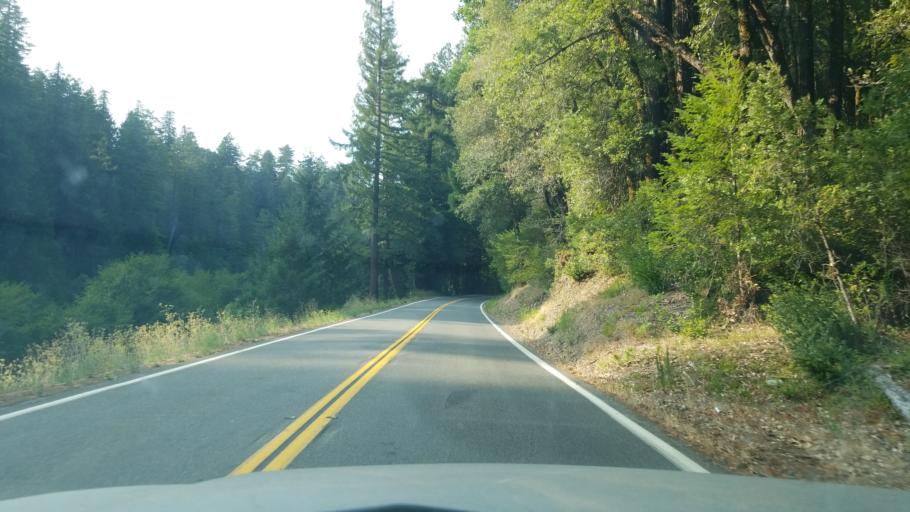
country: US
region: California
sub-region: Humboldt County
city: Redway
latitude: 40.2755
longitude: -123.8517
